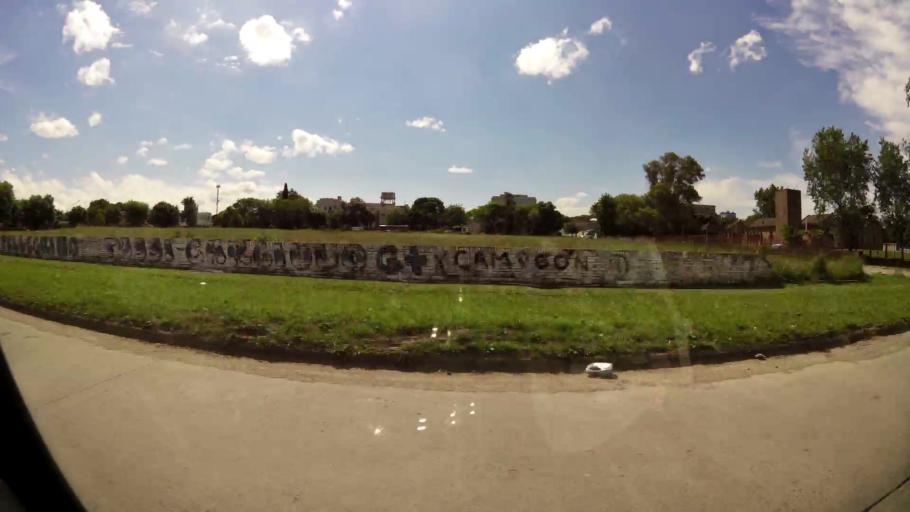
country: AR
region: Buenos Aires
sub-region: Partido de La Plata
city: La Plata
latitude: -34.9241
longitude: -57.9215
